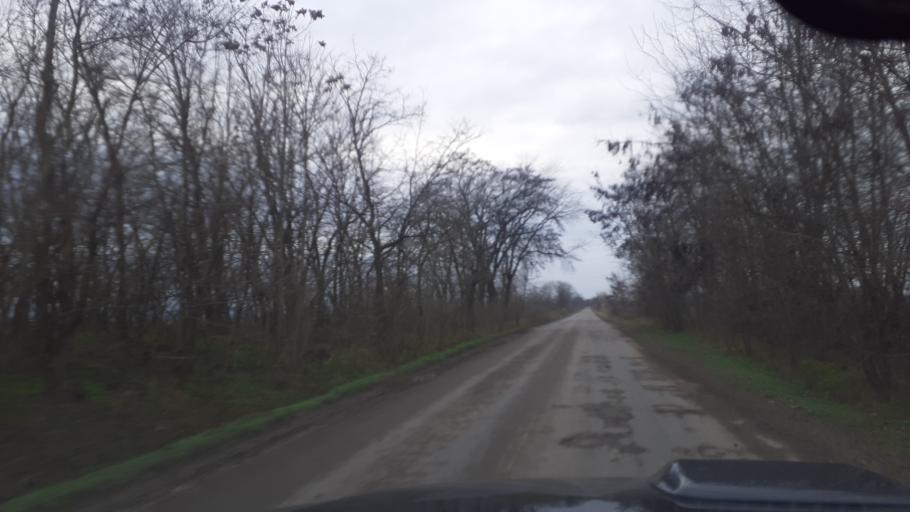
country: HU
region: Bacs-Kiskun
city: Szalkszentmarton
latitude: 46.9540
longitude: 19.0513
